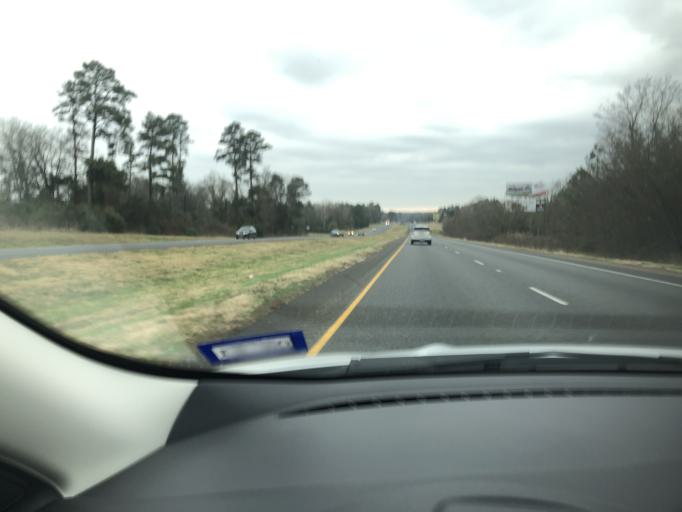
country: US
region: Texas
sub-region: Angelina County
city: Redland
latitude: 31.4887
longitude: -94.7194
